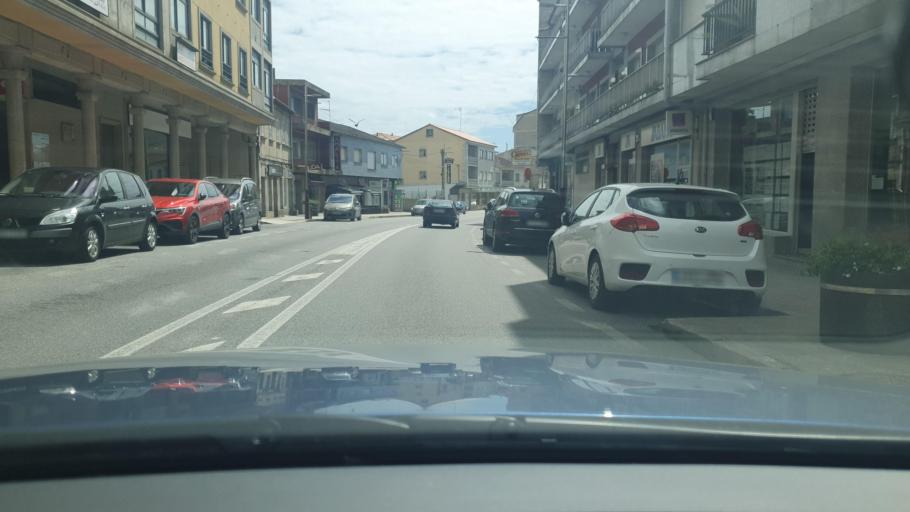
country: ES
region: Galicia
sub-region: Provincia de Pontevedra
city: Meano
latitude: 42.4504
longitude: -8.8128
